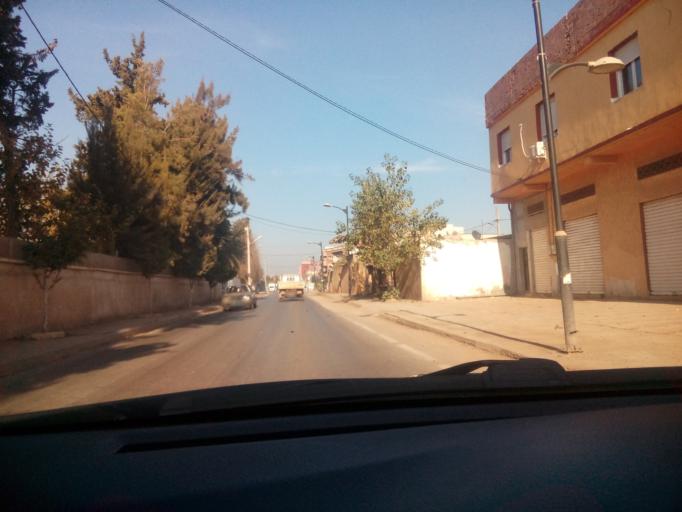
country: DZ
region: Oran
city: Es Senia
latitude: 35.6434
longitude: -0.6268
